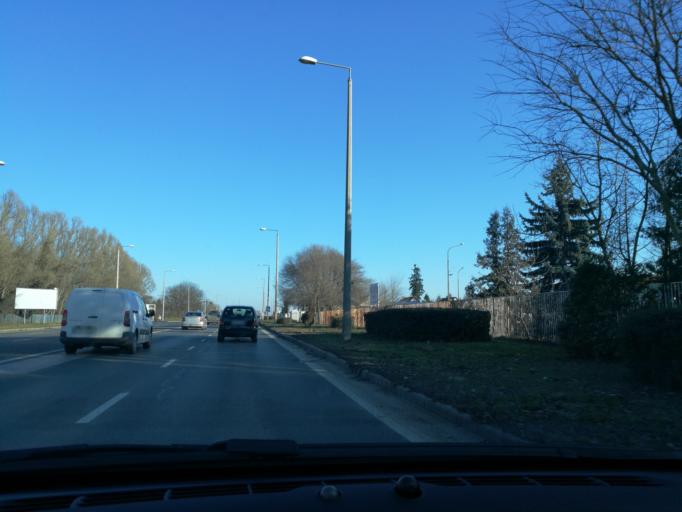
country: HU
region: Szabolcs-Szatmar-Bereg
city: Nyiregyhaza
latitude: 47.9519
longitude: 21.7462
